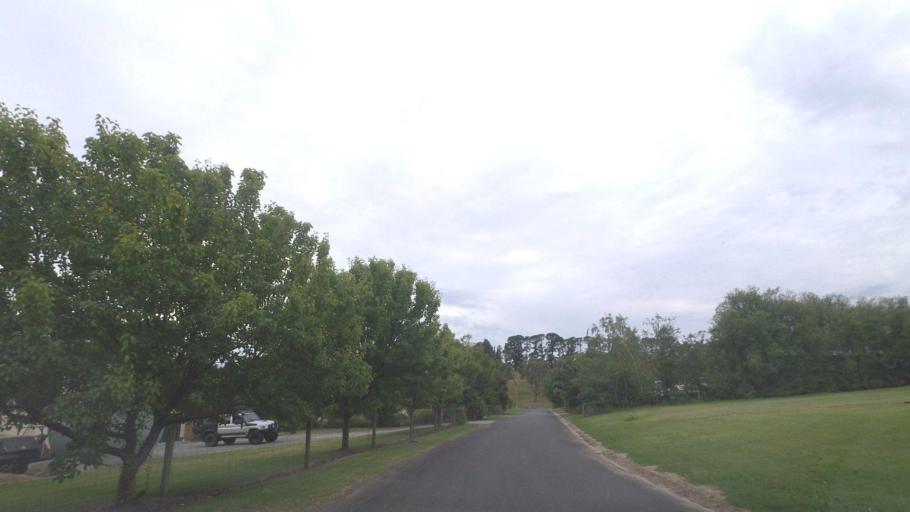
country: AU
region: Victoria
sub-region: Yarra Ranges
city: Lilydale
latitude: -37.7547
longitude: 145.3781
